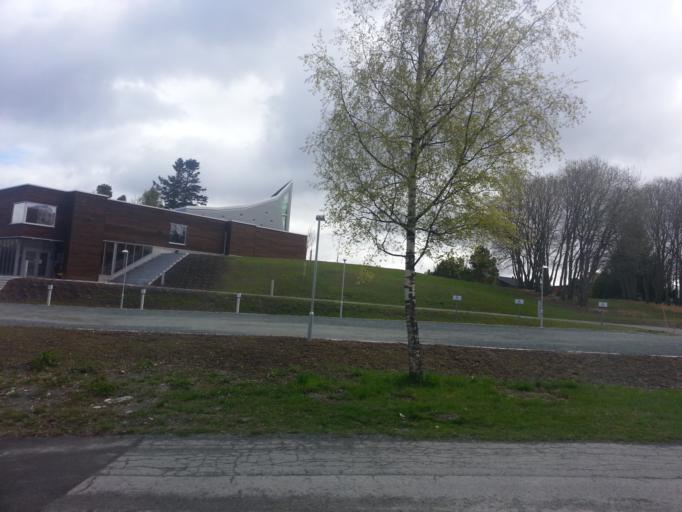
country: NO
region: Sor-Trondelag
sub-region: Trondheim
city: Trondheim
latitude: 63.4147
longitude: 10.3525
